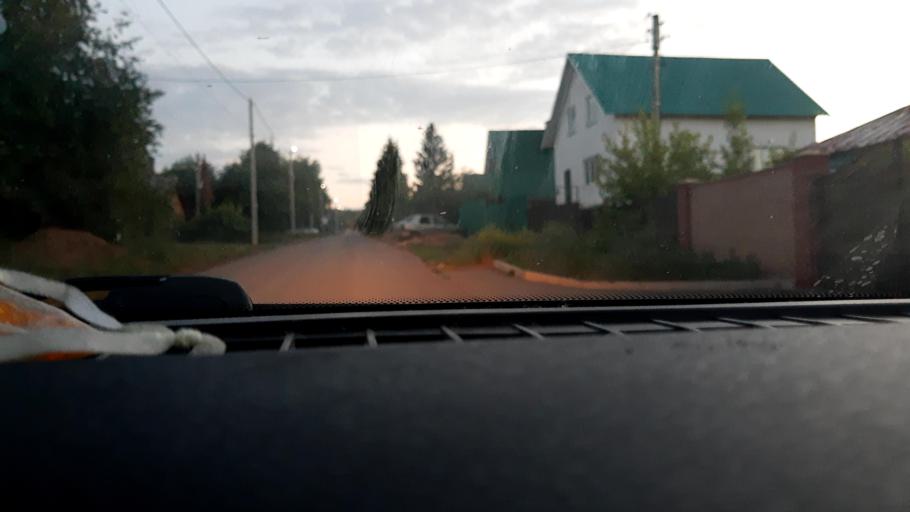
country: RU
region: Bashkortostan
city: Avdon
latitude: 54.6182
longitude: 55.6463
